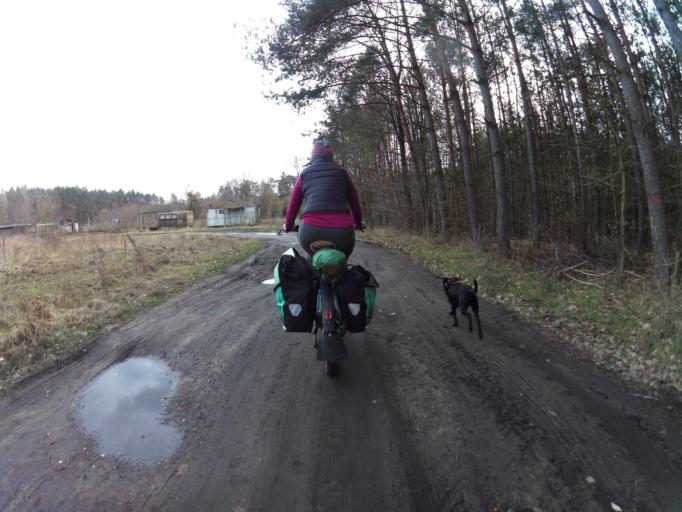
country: PL
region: Lubusz
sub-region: Powiat gorzowski
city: Lubiszyn
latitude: 52.7684
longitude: 14.8371
